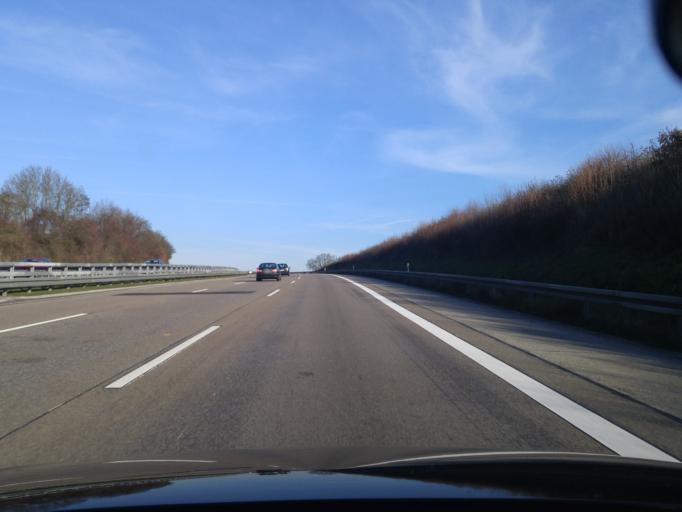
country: DE
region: Hesse
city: Bad Camberg
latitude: 50.2599
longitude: 8.2495
